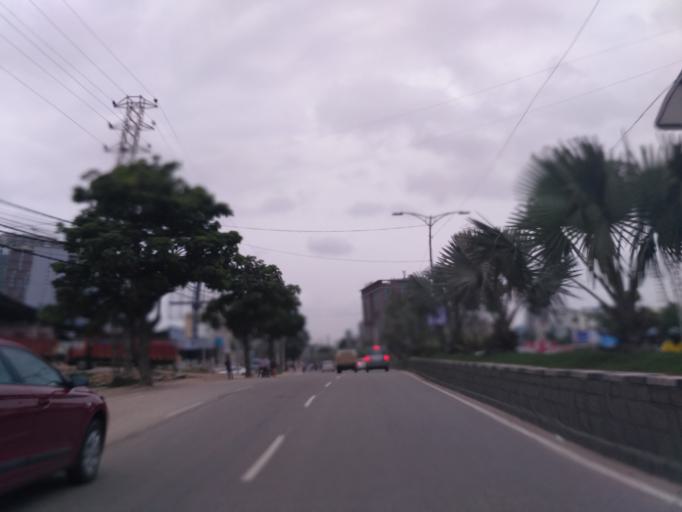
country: IN
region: Telangana
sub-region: Rangareddi
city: Kukatpalli
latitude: 17.4331
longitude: 78.3699
